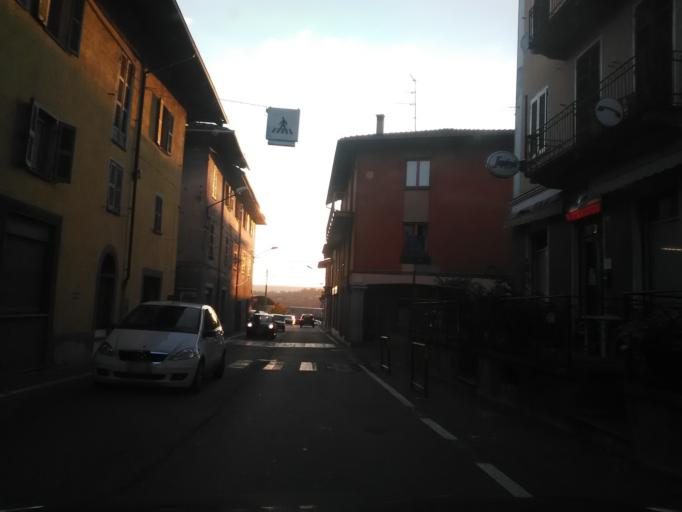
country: IT
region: Piedmont
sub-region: Provincia di Biella
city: Occhieppo Inferiore
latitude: 45.5545
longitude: 8.0204
